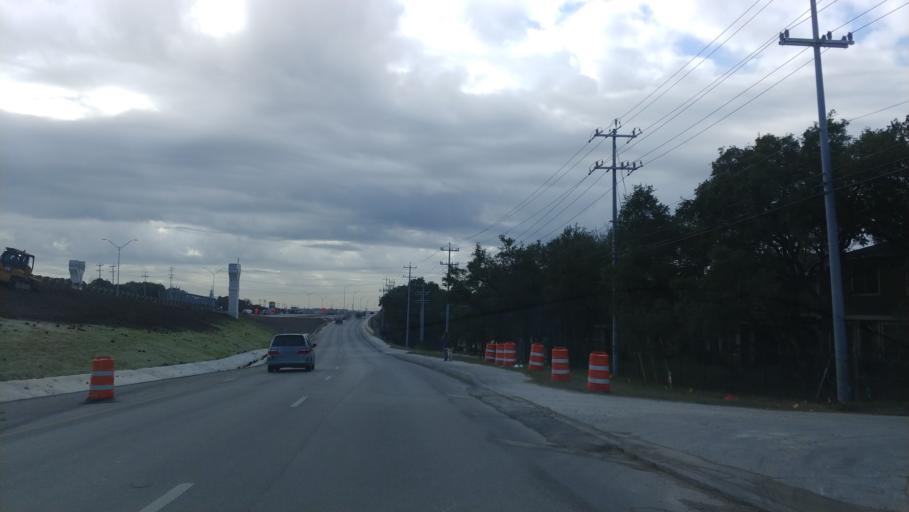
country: US
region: Texas
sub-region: Bexar County
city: Leon Valley
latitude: 29.4468
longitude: -98.7121
